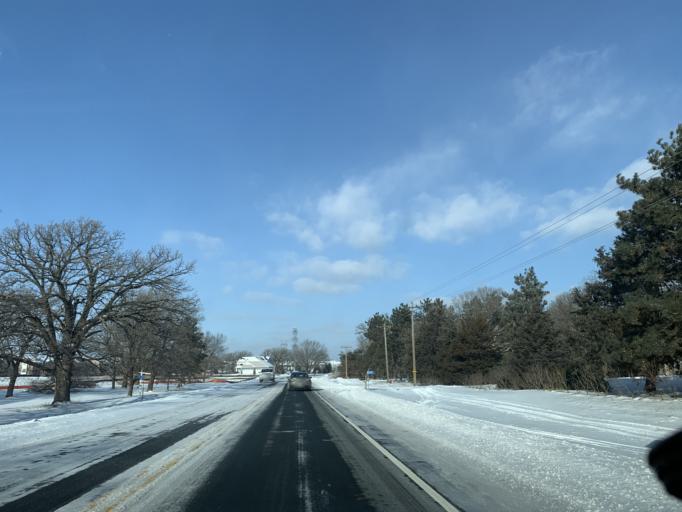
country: US
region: Minnesota
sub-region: Scott County
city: Prior Lake
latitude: 44.7726
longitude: -93.4064
